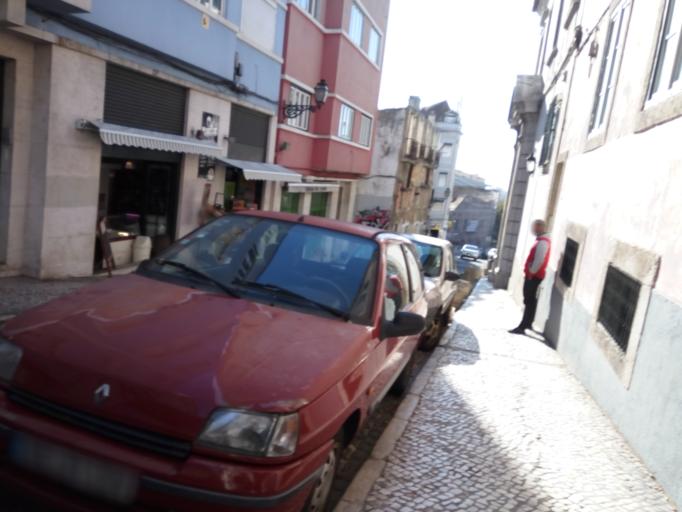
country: PT
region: Lisbon
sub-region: Lisbon
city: Lisbon
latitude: 38.7150
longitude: -9.1311
